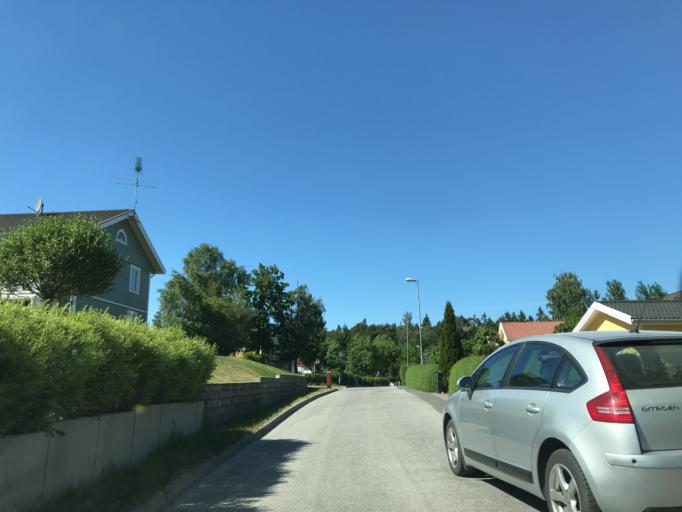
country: SE
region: Stockholm
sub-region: Upplands Vasby Kommun
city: Upplands Vaesby
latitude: 59.4631
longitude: 17.8882
